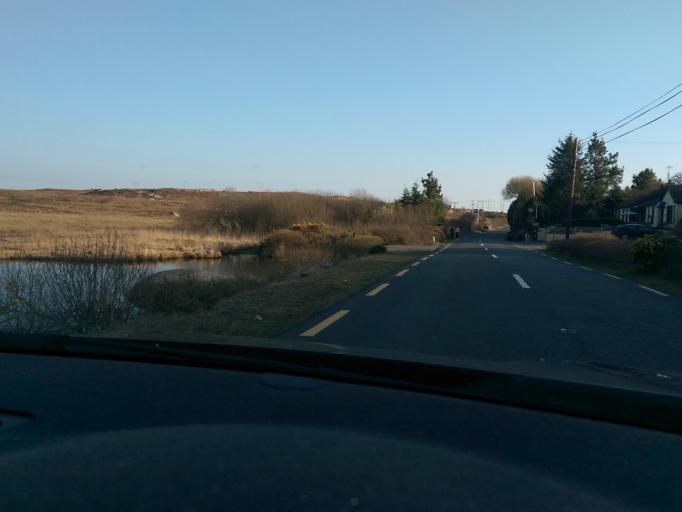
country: IE
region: Connaught
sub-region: County Galway
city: Oughterard
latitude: 53.3696
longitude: -9.5433
